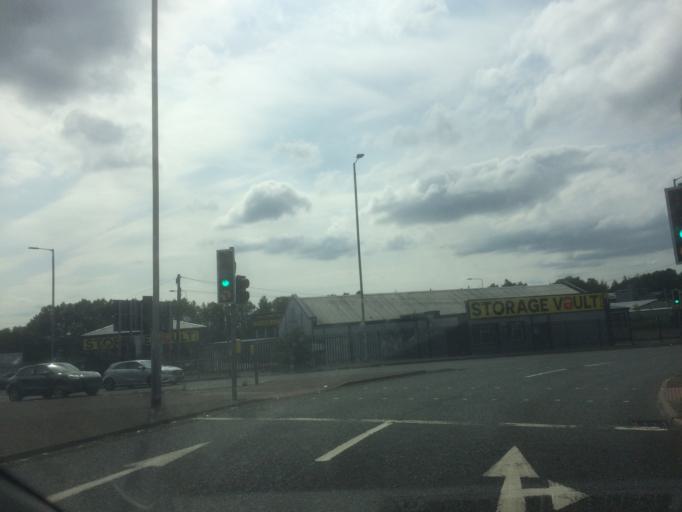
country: GB
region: Scotland
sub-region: South Lanarkshire
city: Rutherglen
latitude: 55.8350
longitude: -4.1717
